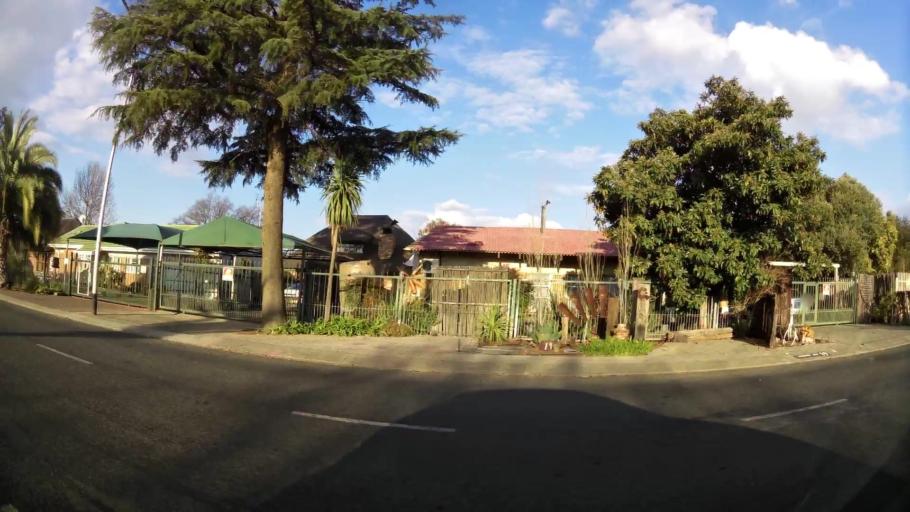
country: ZA
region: Orange Free State
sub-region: Mangaung Metropolitan Municipality
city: Bloemfontein
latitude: -29.1471
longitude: 26.1881
